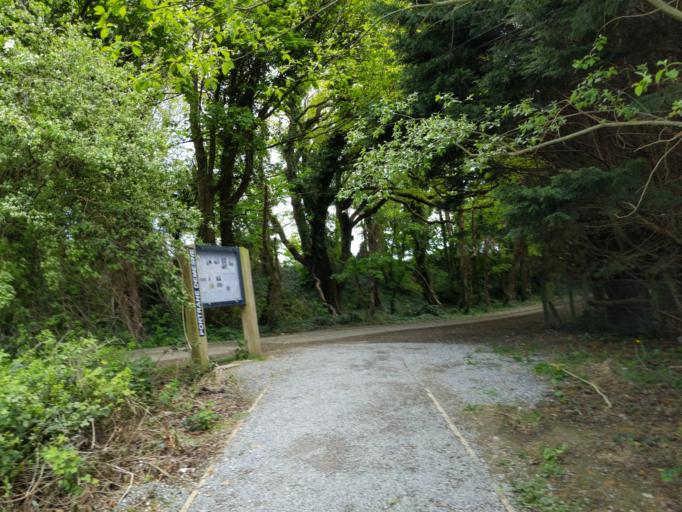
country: IE
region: Leinster
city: Portraine
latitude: 53.4867
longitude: -6.1171
